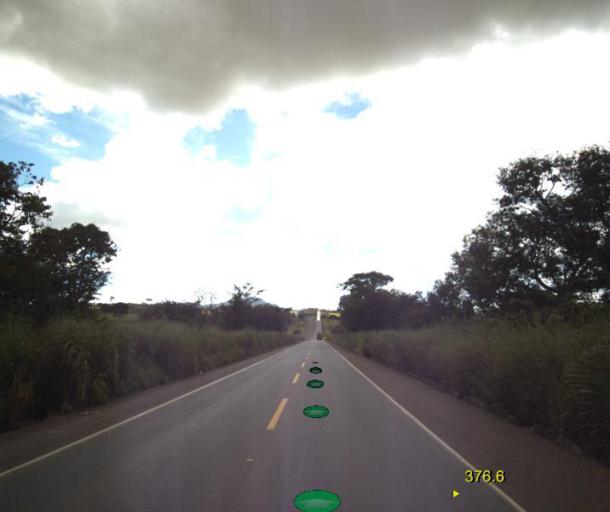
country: BR
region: Goias
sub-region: Jaragua
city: Jaragua
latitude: -15.8728
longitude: -49.2521
